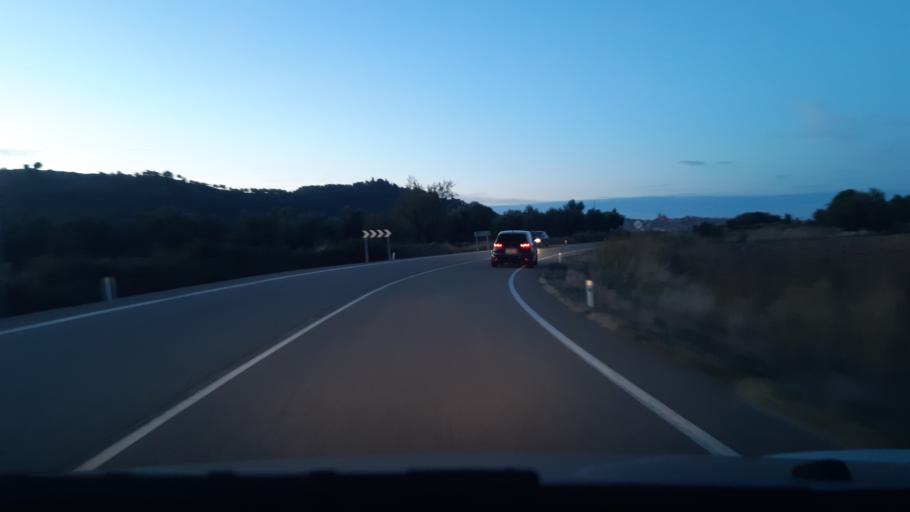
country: ES
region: Aragon
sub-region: Provincia de Teruel
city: Calaceite
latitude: 41.0012
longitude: 0.1937
